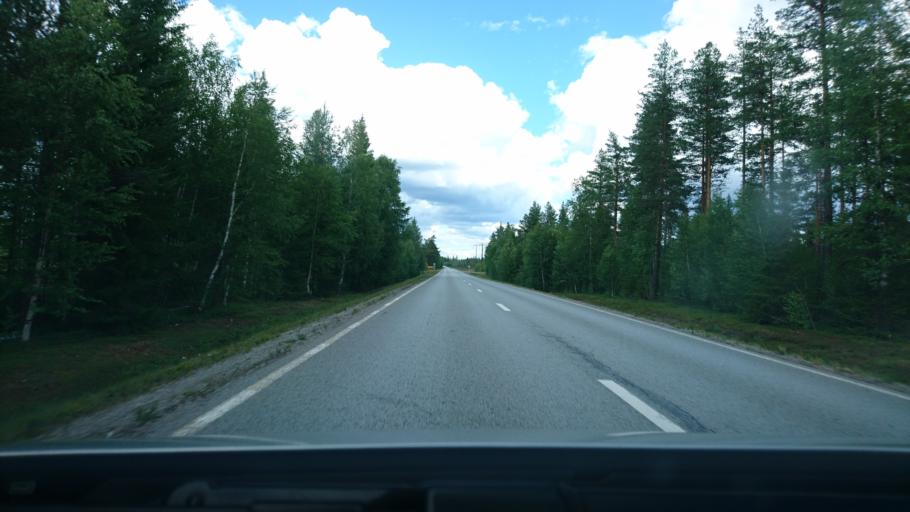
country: SE
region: Vaesterbotten
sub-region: Asele Kommun
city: Asele
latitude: 63.7377
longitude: 16.9946
